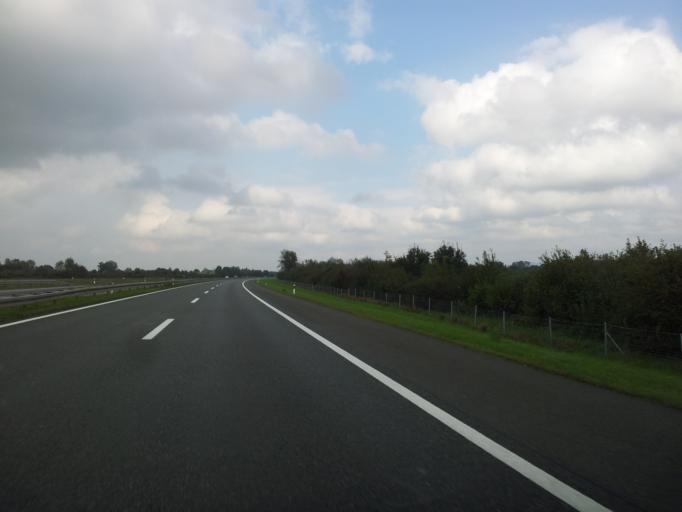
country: HR
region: Brodsko-Posavska
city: Okucani
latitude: 45.2343
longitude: 17.1995
